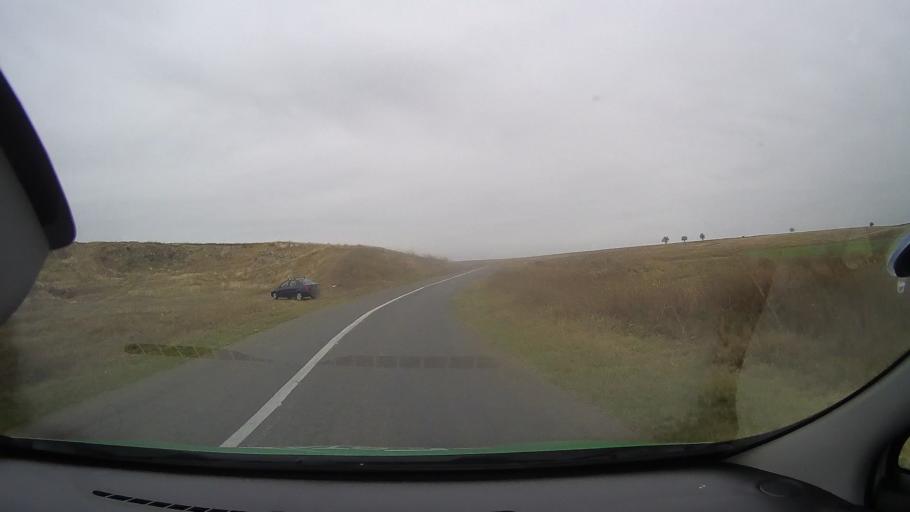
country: RO
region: Constanta
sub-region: Comuna Saraiu
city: Saraiu
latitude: 44.7268
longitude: 28.1751
